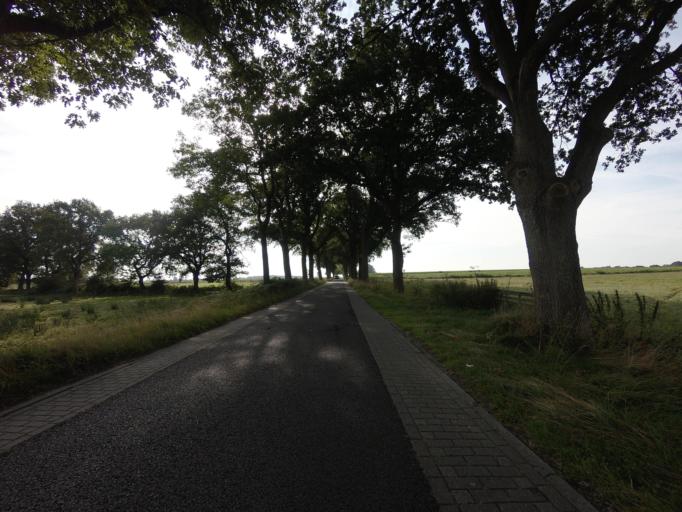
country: NL
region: Drenthe
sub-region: Gemeente Assen
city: Assen
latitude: 53.0078
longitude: 6.6177
